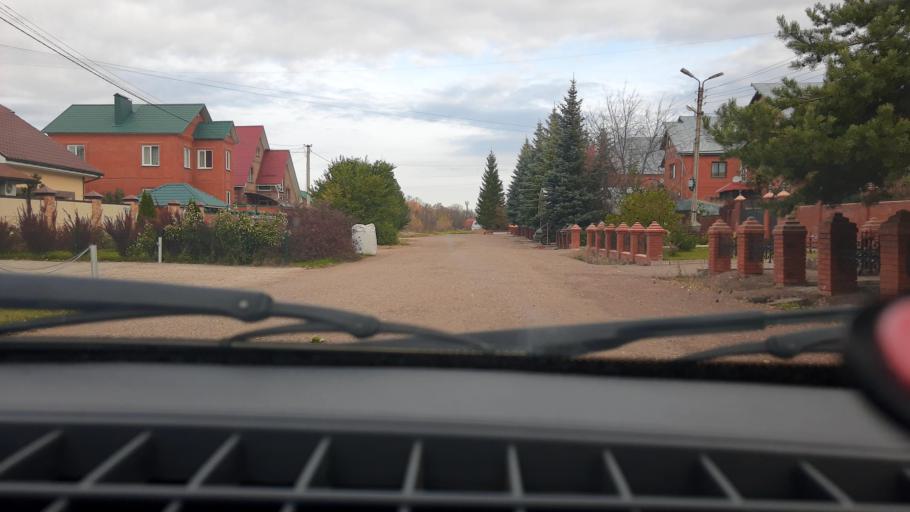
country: RU
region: Bashkortostan
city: Mikhaylovka
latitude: 54.7956
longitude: 55.9432
